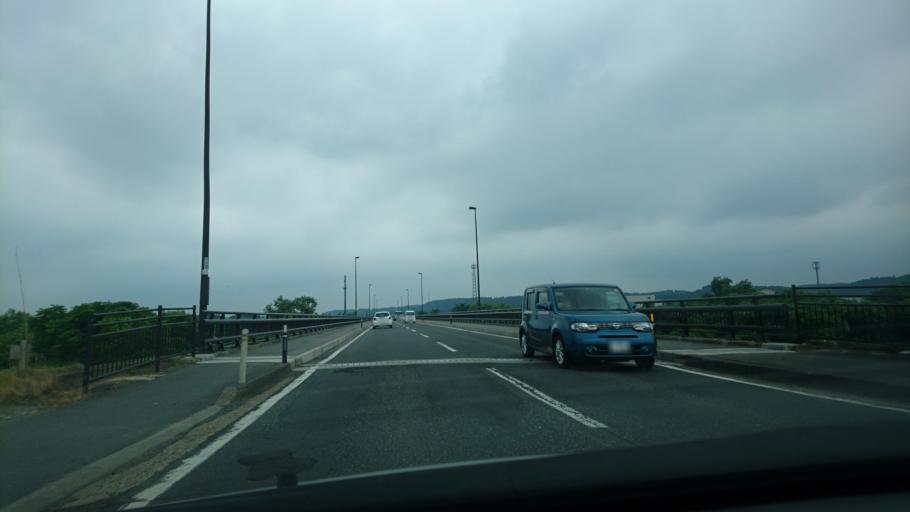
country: JP
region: Miyagi
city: Furukawa
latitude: 38.6551
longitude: 140.8803
